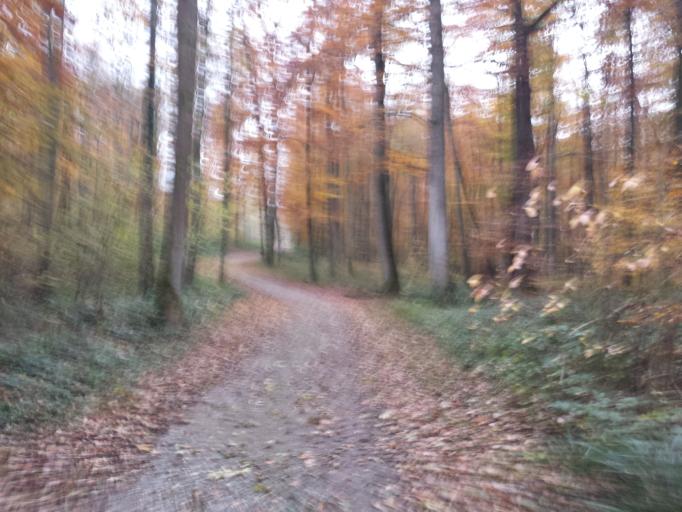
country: CH
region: Thurgau
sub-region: Arbon District
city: Uttwil
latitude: 47.5707
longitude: 9.3525
